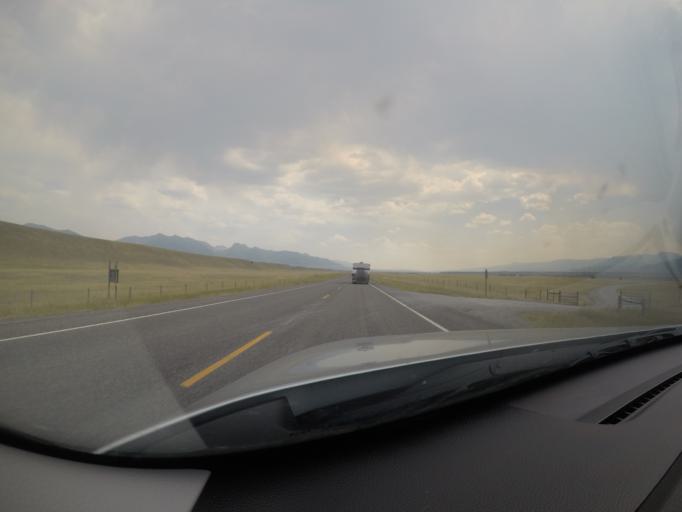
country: US
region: Montana
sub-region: Madison County
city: Virginia City
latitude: 45.1376
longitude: -111.6731
